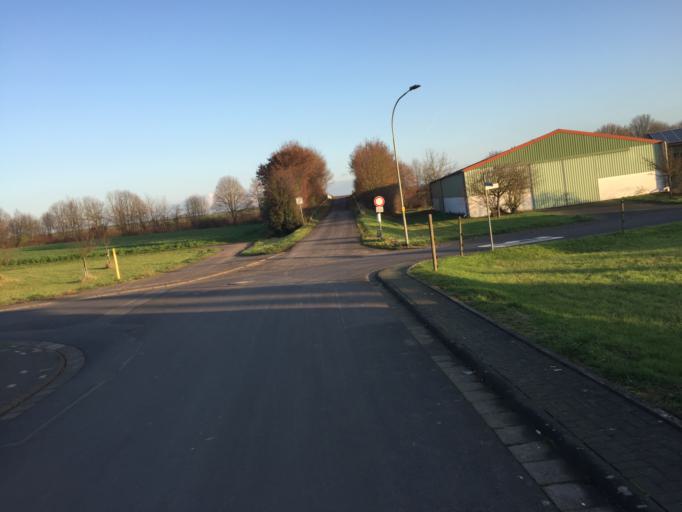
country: DE
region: Hesse
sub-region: Regierungsbezirk Darmstadt
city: Munzenberg
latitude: 50.4788
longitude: 8.7622
